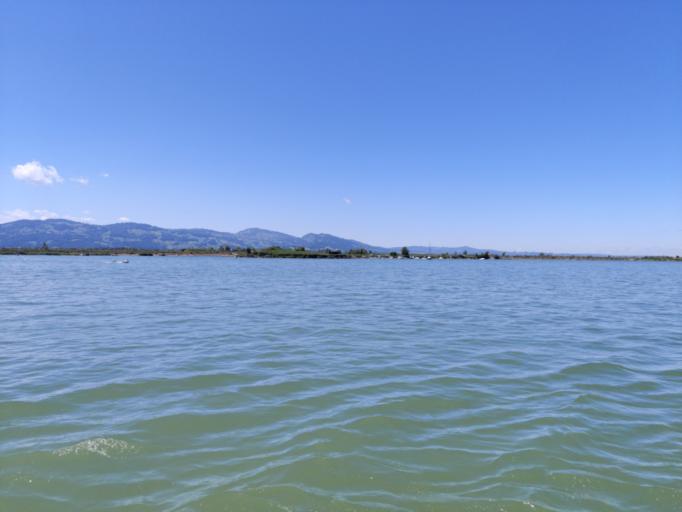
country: AT
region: Vorarlberg
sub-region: Politischer Bezirk Bregenz
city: Fussach
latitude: 47.5151
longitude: 9.6660
